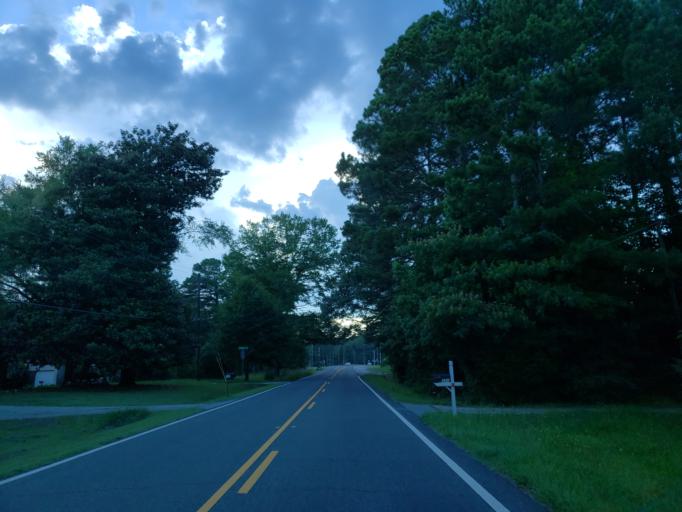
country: US
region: Georgia
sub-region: Bartow County
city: Cartersville
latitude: 34.2014
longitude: -84.7426
